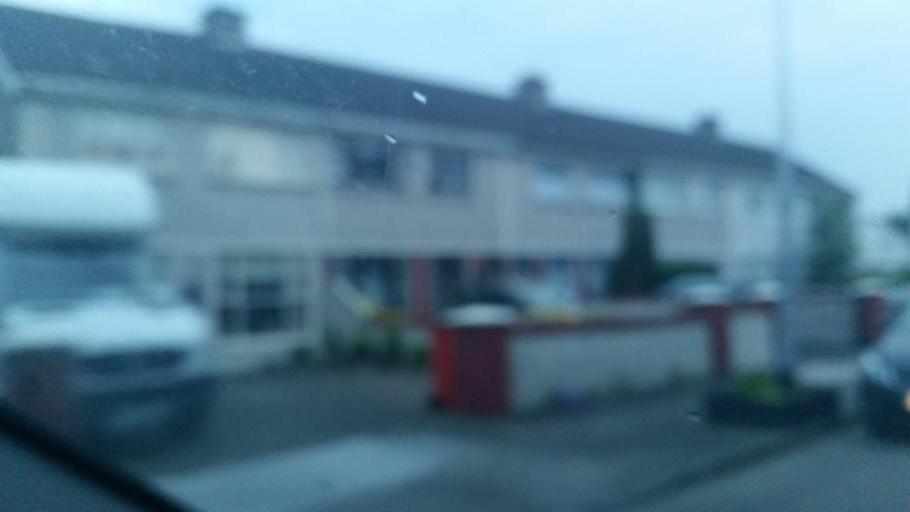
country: IE
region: Leinster
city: Raheny
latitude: 53.3918
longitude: -6.1849
